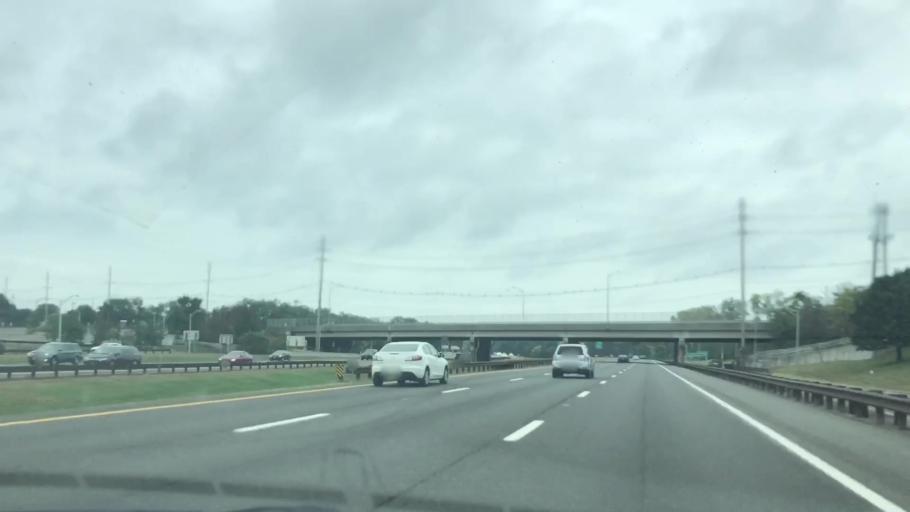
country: US
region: New Jersey
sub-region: Bergen County
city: Paramus
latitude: 40.9621
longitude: -74.0654
